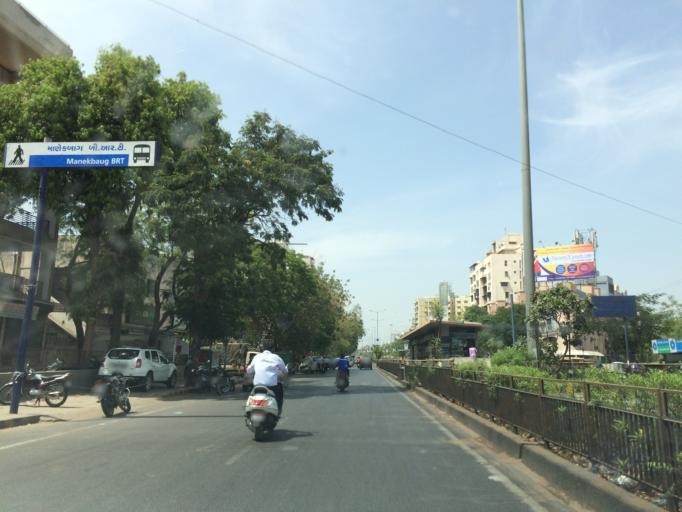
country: IN
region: Gujarat
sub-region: Ahmadabad
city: Ahmedabad
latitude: 23.0178
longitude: 72.5441
